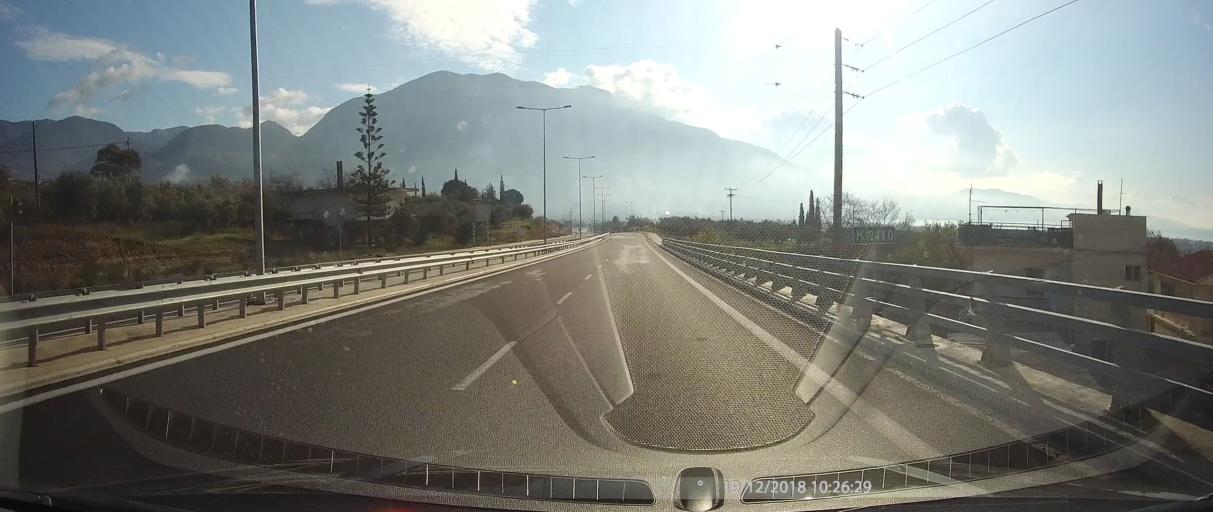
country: GR
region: Peloponnese
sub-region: Nomos Messinias
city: Kalamata
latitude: 37.0447
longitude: 22.1275
